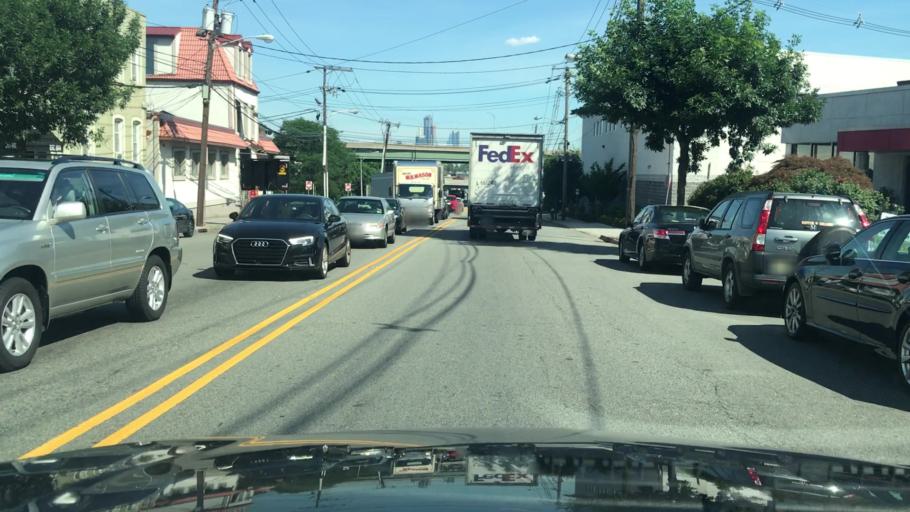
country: US
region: New Jersey
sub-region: Hudson County
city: Secaucus
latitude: 40.7874
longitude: -74.0537
